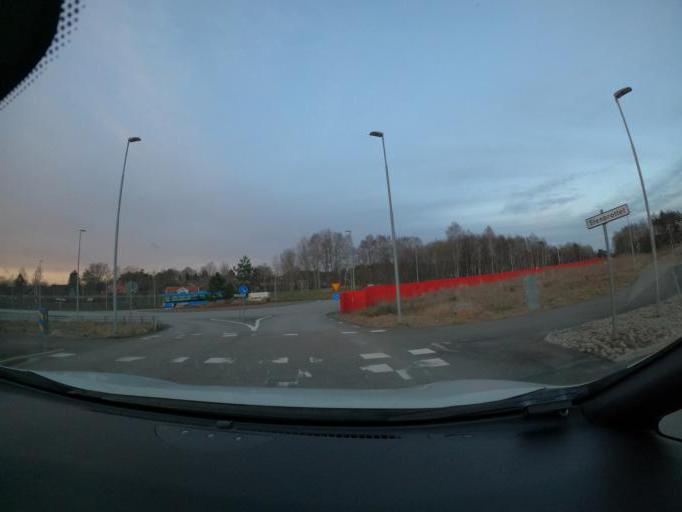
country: SE
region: Vaestra Goetaland
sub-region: Harryda Kommun
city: Molnlycke
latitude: 57.6541
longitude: 12.1289
